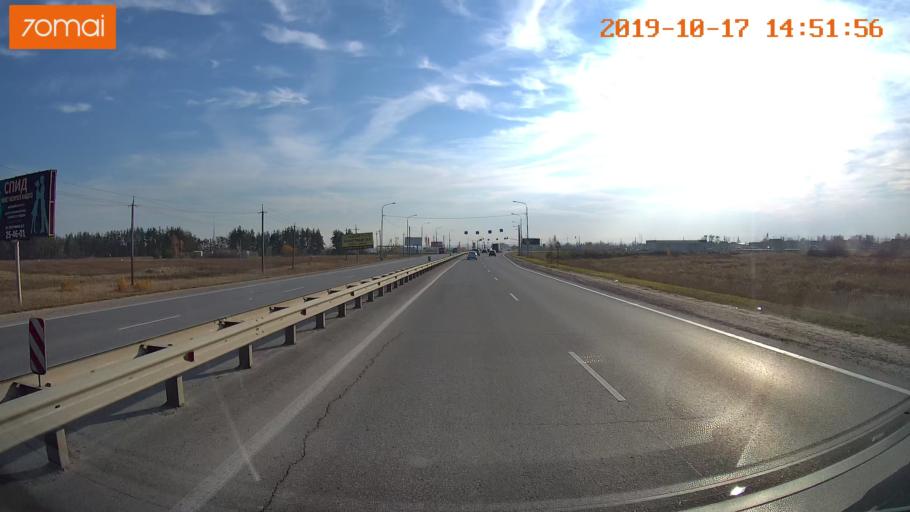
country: RU
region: Rjazan
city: Polyany
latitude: 54.7118
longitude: 39.8475
